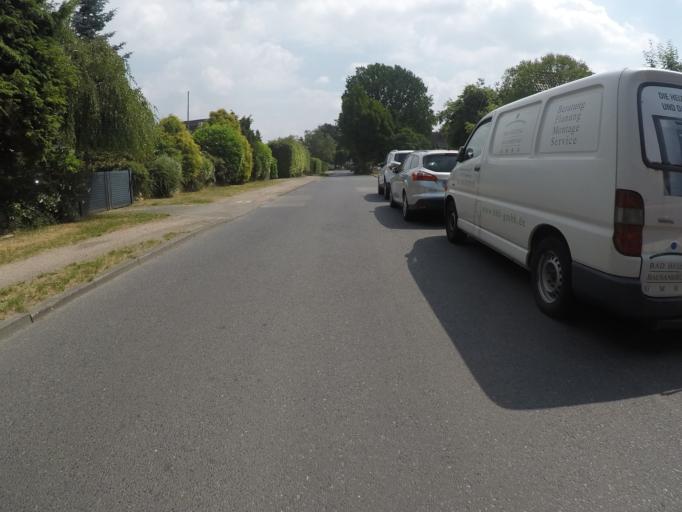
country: DE
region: Hamburg
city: Sasel
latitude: 53.6433
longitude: 10.1214
